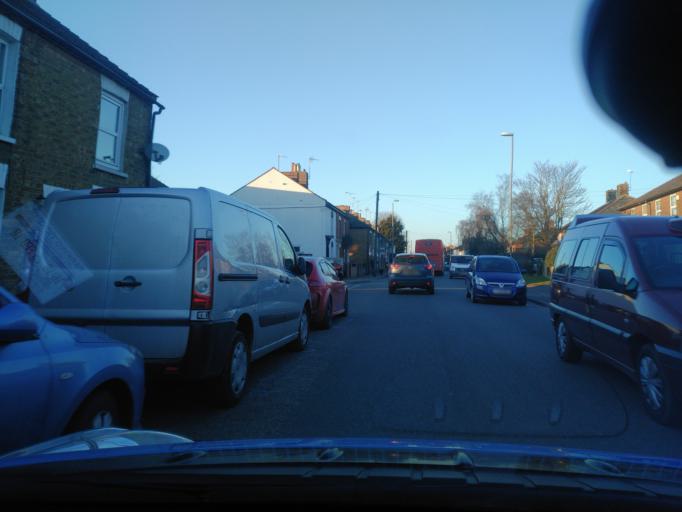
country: GB
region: England
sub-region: Central Bedfordshire
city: Toddington
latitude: 51.9442
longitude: -0.5338
